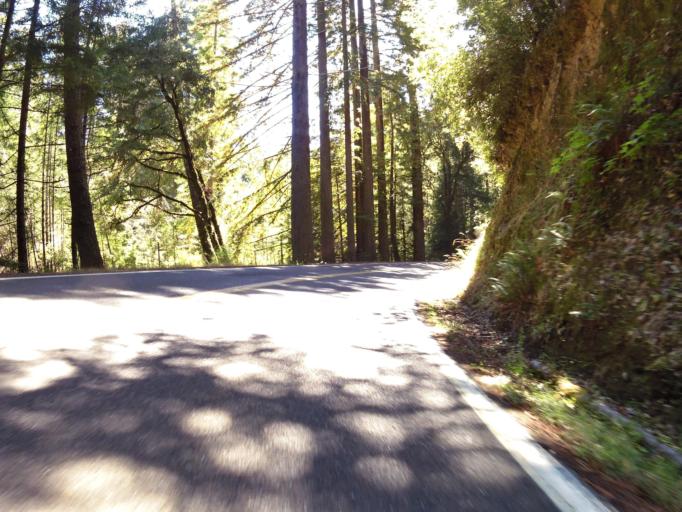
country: US
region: California
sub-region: Humboldt County
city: Redway
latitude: 39.8186
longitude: -123.7809
